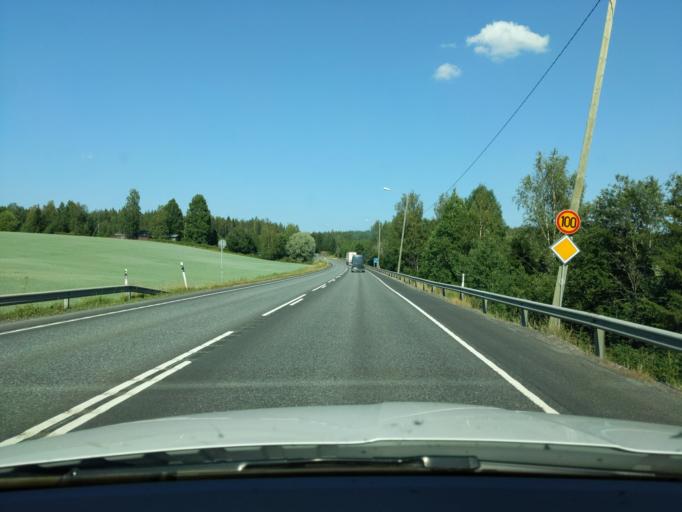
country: FI
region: Paijanne Tavastia
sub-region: Lahti
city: Hollola
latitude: 60.9502
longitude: 25.4258
